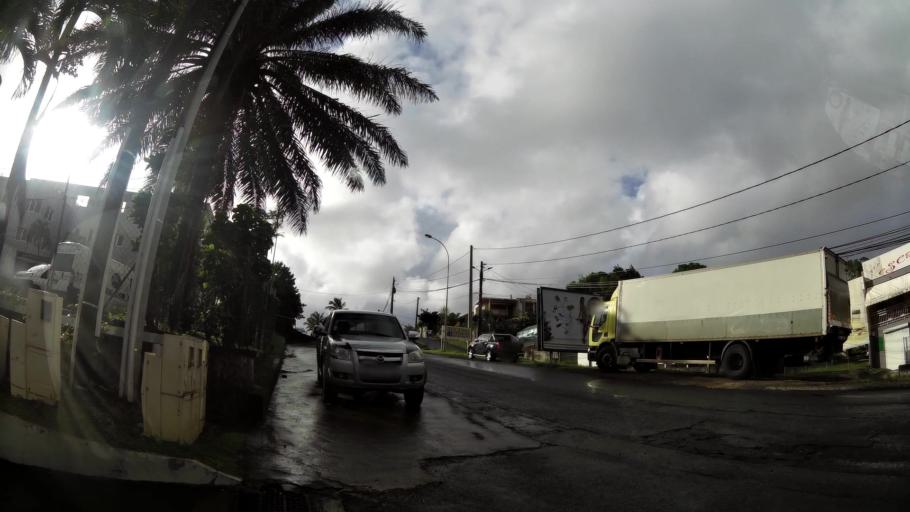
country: MQ
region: Martinique
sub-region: Martinique
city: Le Lamentin
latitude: 14.6191
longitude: -61.0398
